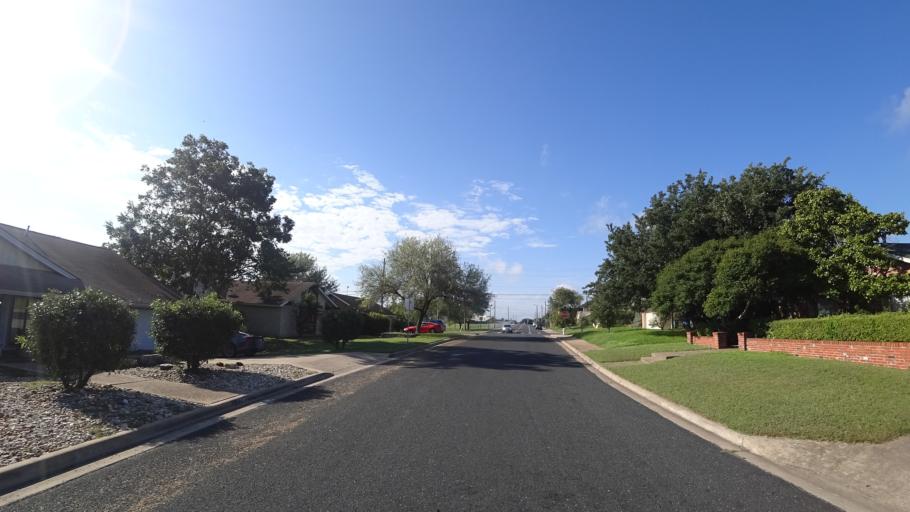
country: US
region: Texas
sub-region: Travis County
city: Austin
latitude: 30.3274
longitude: -97.6875
